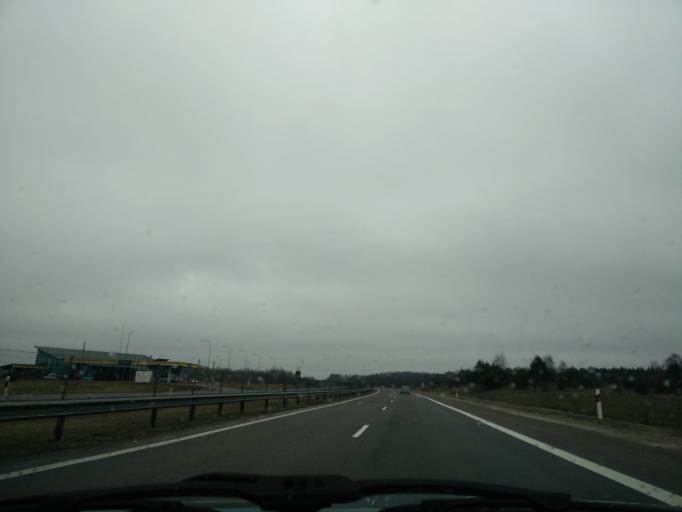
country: LT
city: Skaudvile
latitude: 55.4130
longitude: 22.8249
